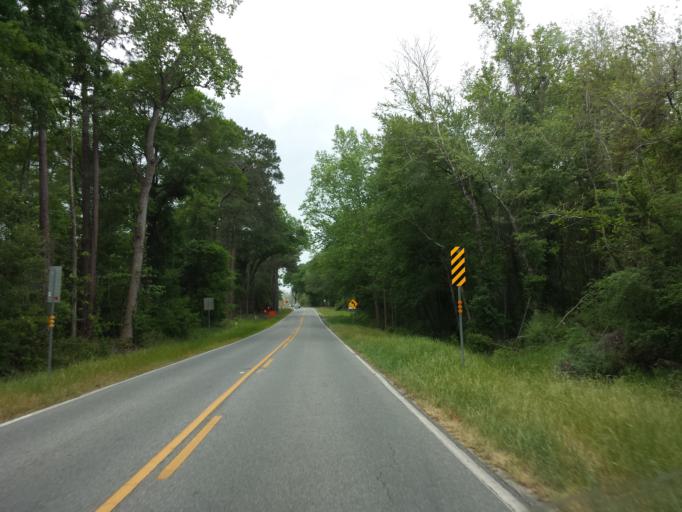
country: US
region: Georgia
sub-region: Cook County
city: Sparks
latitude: 31.2774
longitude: -83.4663
